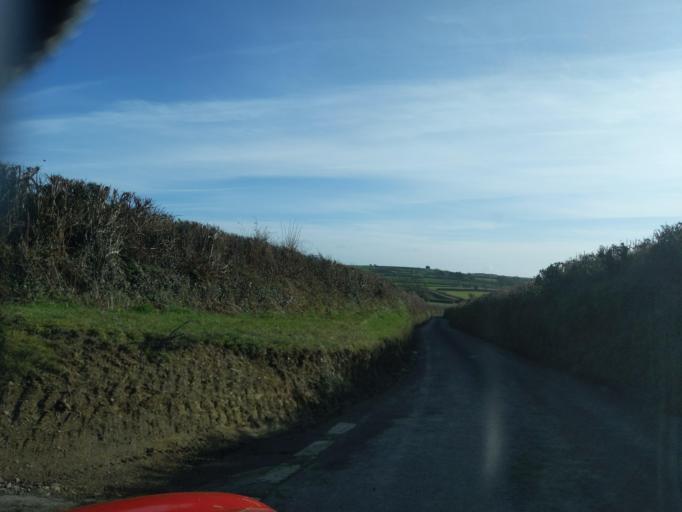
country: GB
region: England
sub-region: Devon
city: Kingsbridge
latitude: 50.3391
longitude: -3.7230
